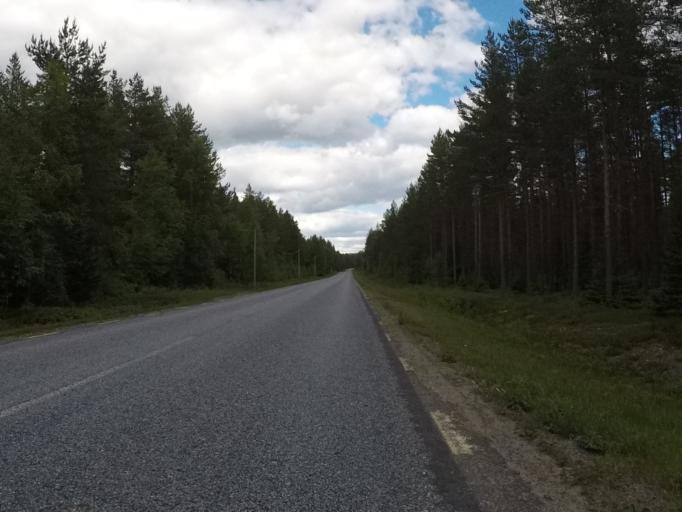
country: SE
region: Vaesterbotten
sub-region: Umea Kommun
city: Saevar
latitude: 63.9465
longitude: 20.7906
